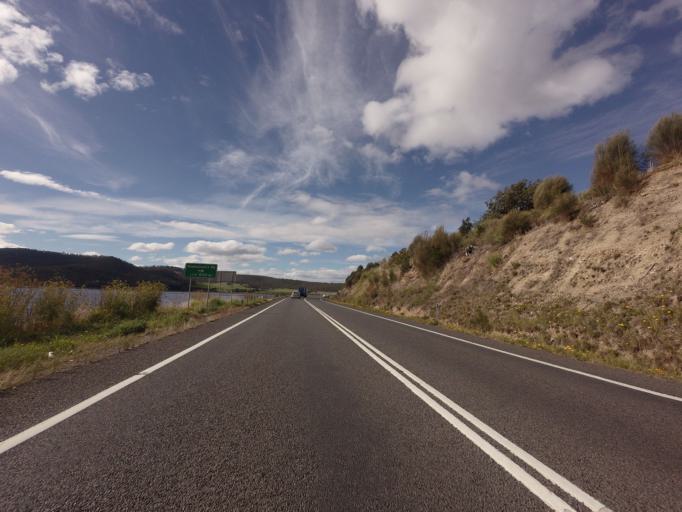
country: AU
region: Tasmania
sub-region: Brighton
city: Bridgewater
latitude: -42.7422
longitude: 147.1938
